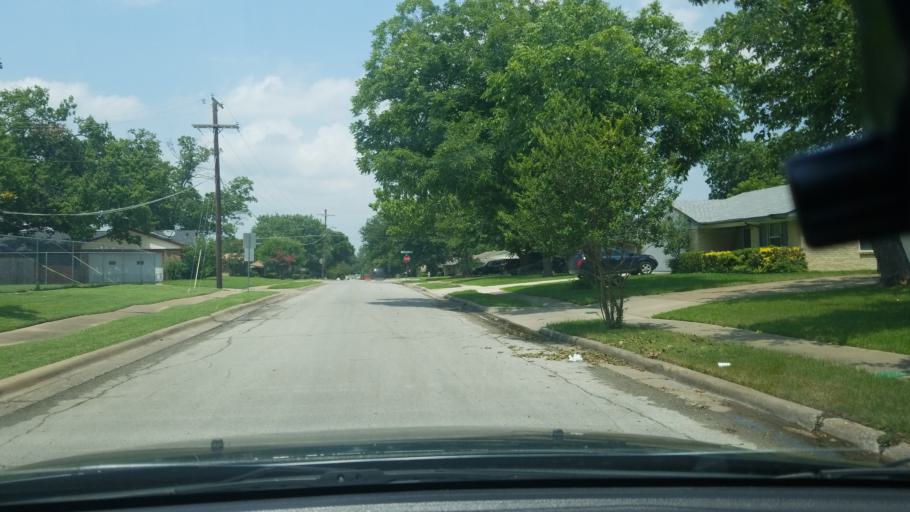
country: US
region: Texas
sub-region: Dallas County
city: Mesquite
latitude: 32.8023
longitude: -96.6405
